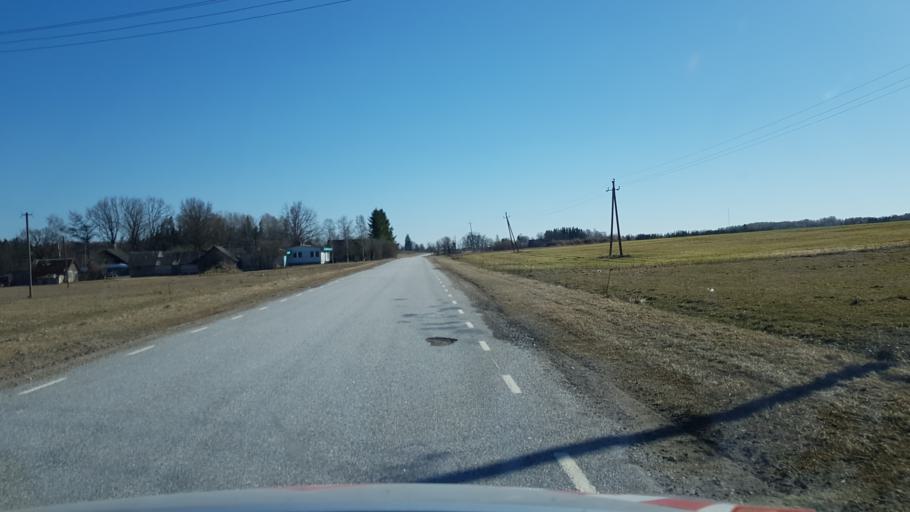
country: EE
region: Jaervamaa
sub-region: Koeru vald
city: Koeru
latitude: 59.0453
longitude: 26.0900
